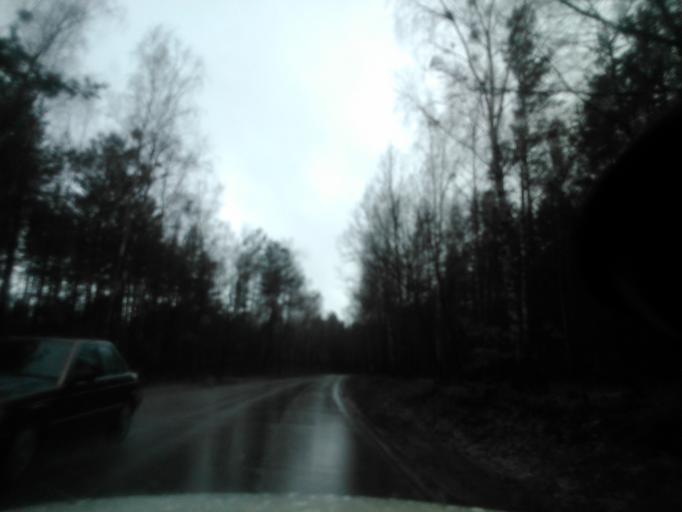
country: PL
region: Warmian-Masurian Voivodeship
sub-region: Powiat dzialdowski
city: Rybno
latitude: 53.3240
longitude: 19.9082
